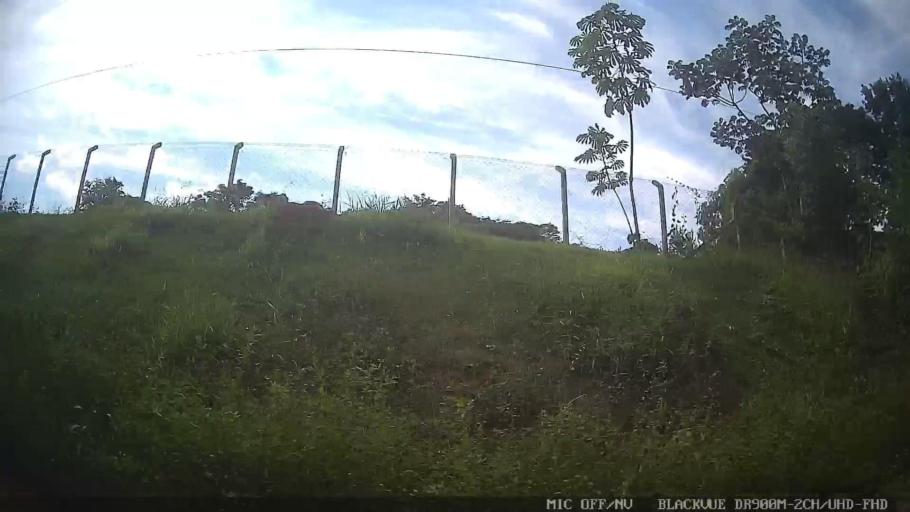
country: BR
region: Sao Paulo
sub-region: Braganca Paulista
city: Braganca Paulista
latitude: -22.9866
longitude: -46.6473
